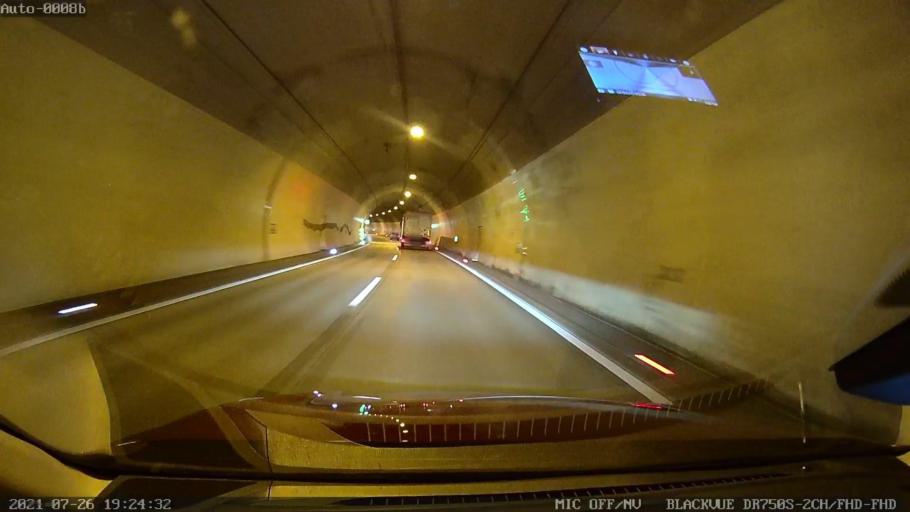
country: AT
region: Upper Austria
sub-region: Politischer Bezirk Kirchdorf an der Krems
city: Micheldorf in Oberoesterreich
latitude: 47.8674
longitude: 14.1302
